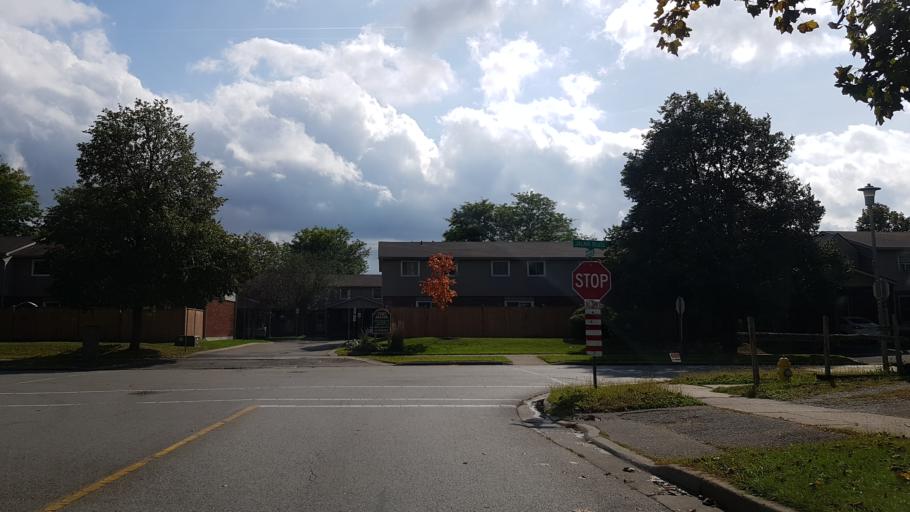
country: CA
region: Ontario
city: London
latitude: 42.9254
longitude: -81.2358
